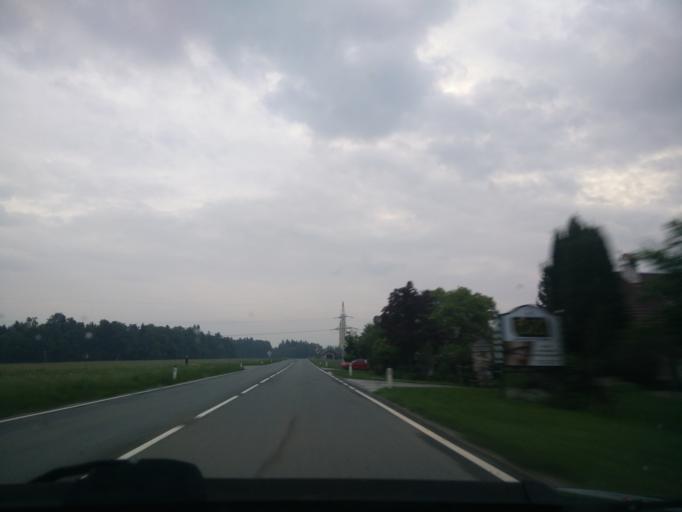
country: AT
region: Salzburg
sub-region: Politischer Bezirk Salzburg-Umgebung
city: Elixhausen
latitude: 47.8954
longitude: 13.0762
